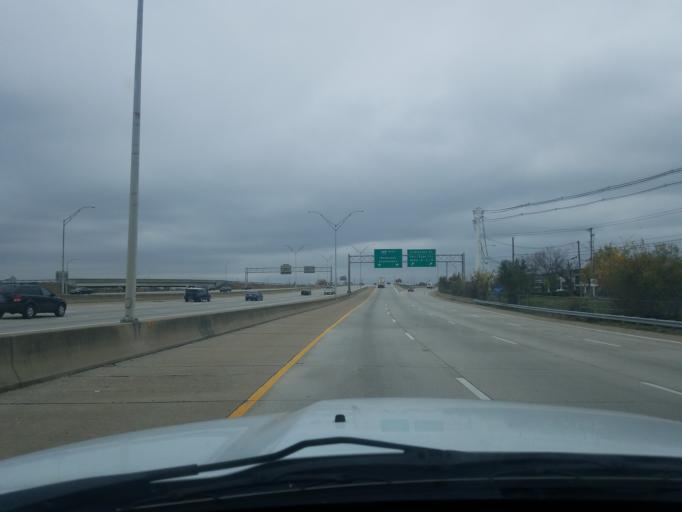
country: US
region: Kentucky
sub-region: Jefferson County
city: Audubon Park
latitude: 38.1898
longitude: -85.7460
